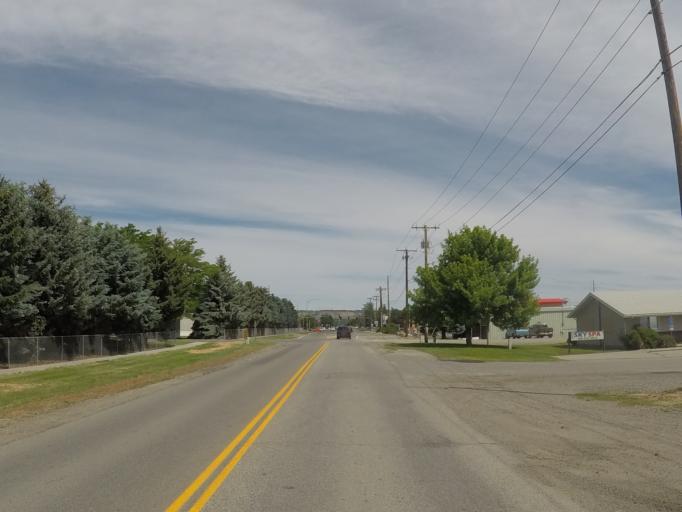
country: US
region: Montana
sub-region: Yellowstone County
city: Billings
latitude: 45.7527
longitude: -108.5968
